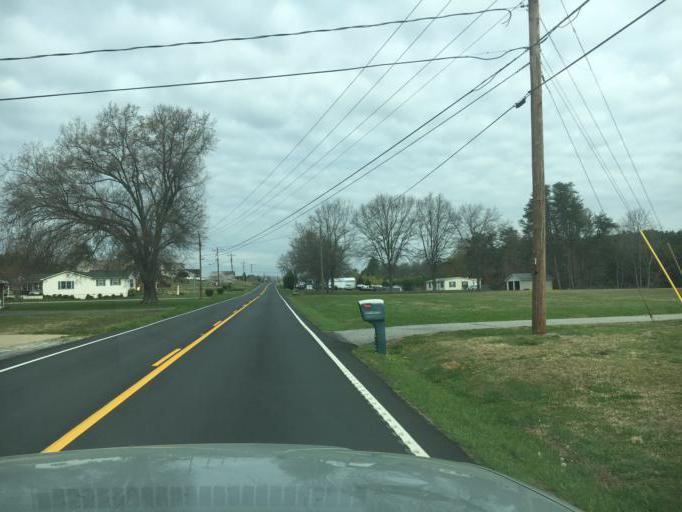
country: US
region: South Carolina
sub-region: Spartanburg County
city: Inman Mills
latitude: 35.0463
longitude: -82.1364
